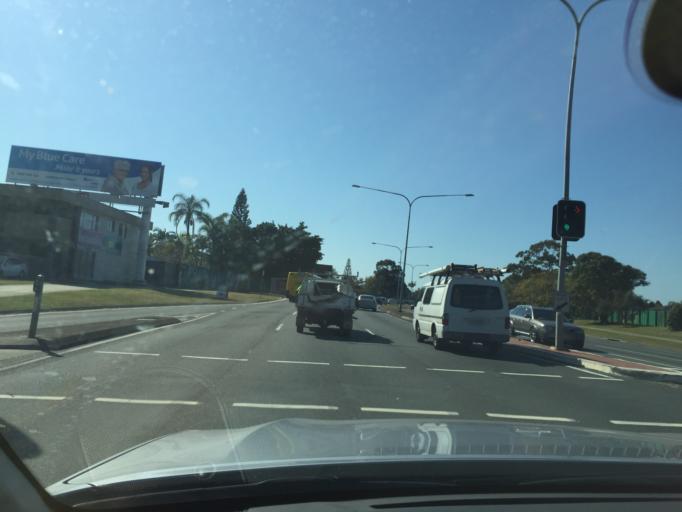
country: AU
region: Queensland
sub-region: Gold Coast
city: Clear Island Waters
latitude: -28.0322
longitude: 153.4031
